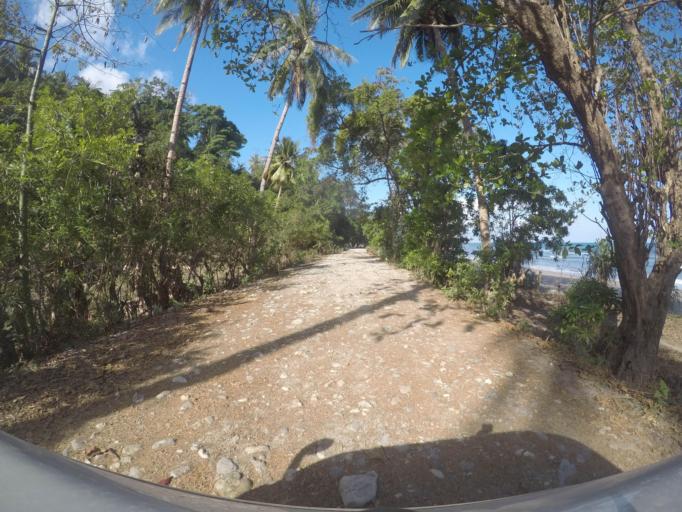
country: TL
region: Viqueque
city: Viqueque
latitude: -8.7999
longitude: 126.5899
